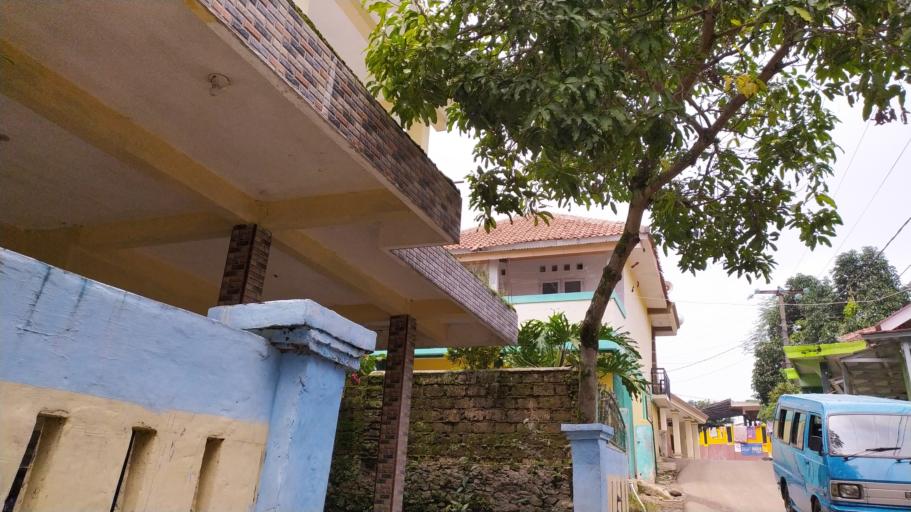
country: ID
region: West Java
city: Ciampea
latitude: -6.6282
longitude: 106.7089
